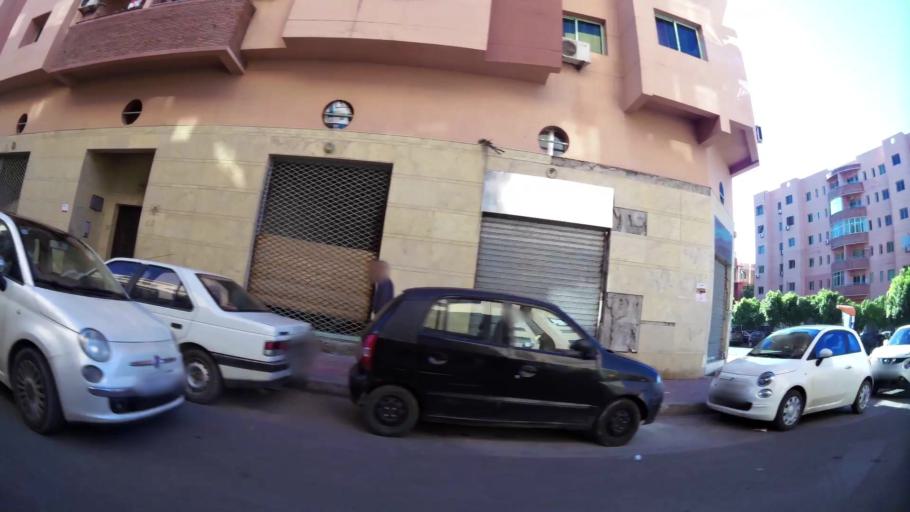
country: MA
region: Marrakech-Tensift-Al Haouz
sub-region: Marrakech
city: Marrakesh
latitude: 31.6512
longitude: -8.0184
